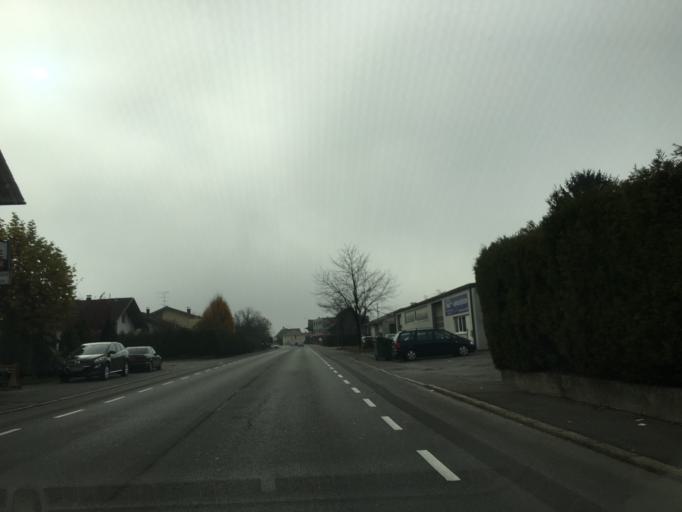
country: AT
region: Vorarlberg
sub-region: Politischer Bezirk Feldkirch
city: Gotzis
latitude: 47.3186
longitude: 9.6224
